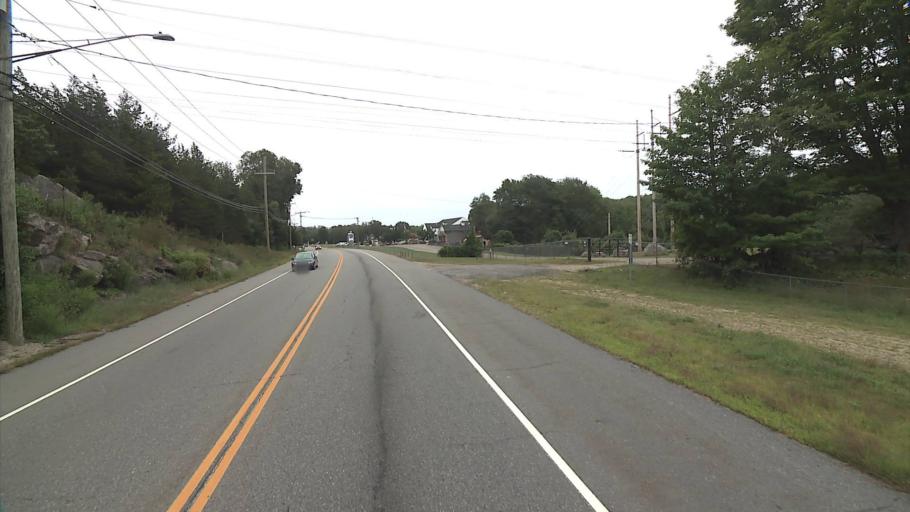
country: US
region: Connecticut
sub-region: New London County
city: Montville Center
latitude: 41.4343
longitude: -72.2237
